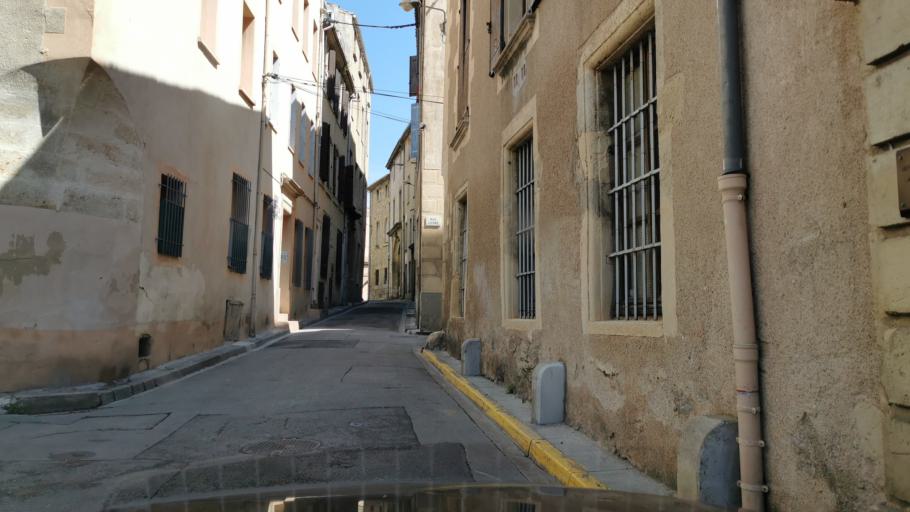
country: FR
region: Languedoc-Roussillon
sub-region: Departement de l'Aude
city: Narbonne
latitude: 43.1843
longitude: 3.0058
